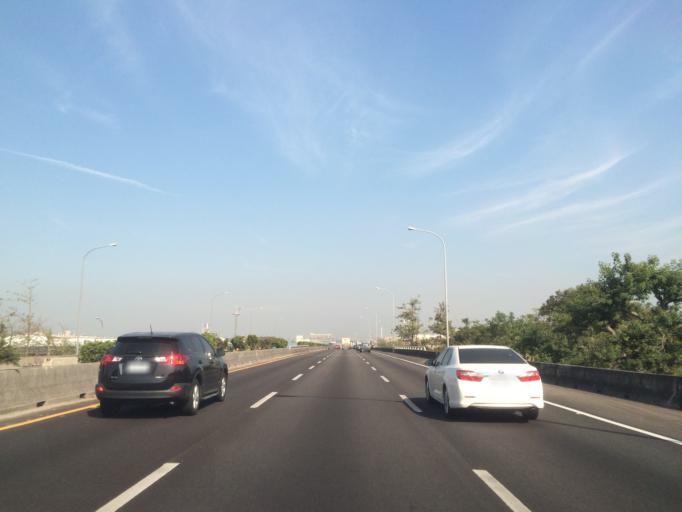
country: TW
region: Taiwan
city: Fengyuan
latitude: 24.2508
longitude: 120.6905
